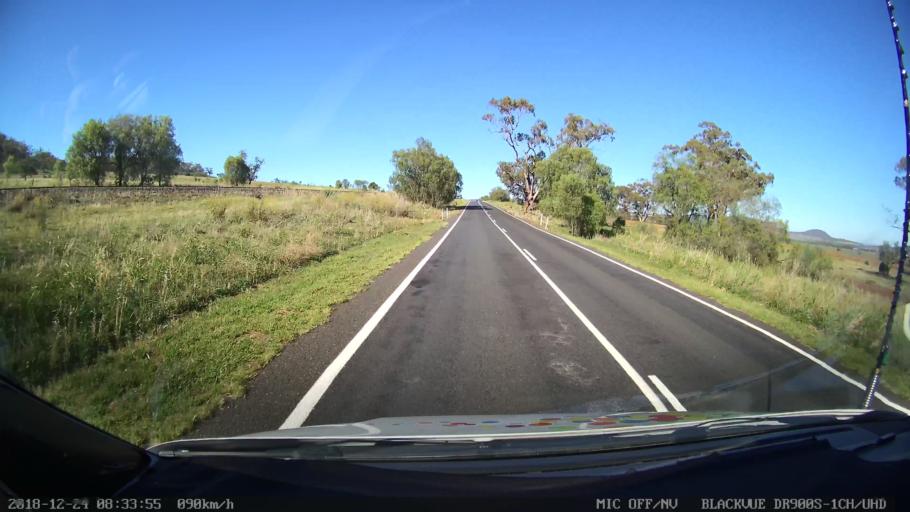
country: AU
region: New South Wales
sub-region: Liverpool Plains
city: Quirindi
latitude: -31.2894
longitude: 150.6779
